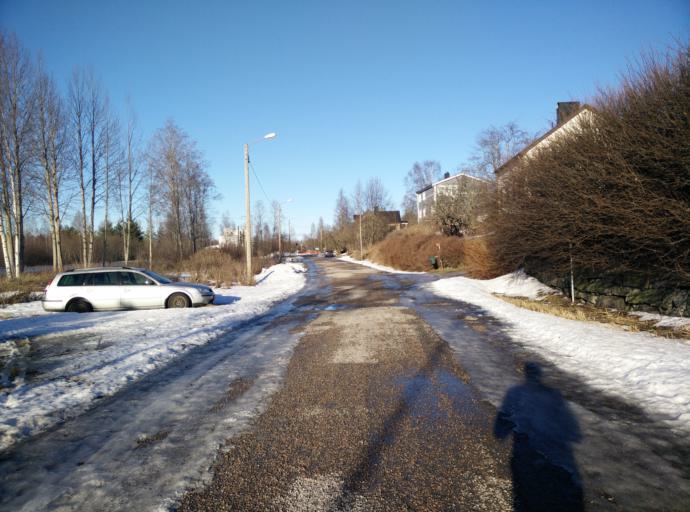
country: SE
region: Vaesternorrland
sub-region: Sundsvalls Kommun
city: Skottsund
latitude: 62.3043
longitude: 17.3848
